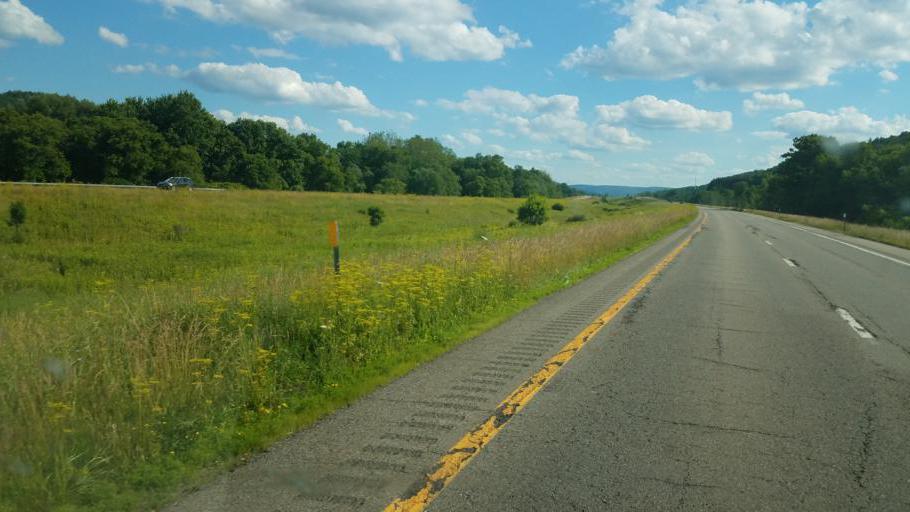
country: US
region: New York
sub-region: Cattaraugus County
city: Olean
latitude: 42.1598
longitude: -78.4026
